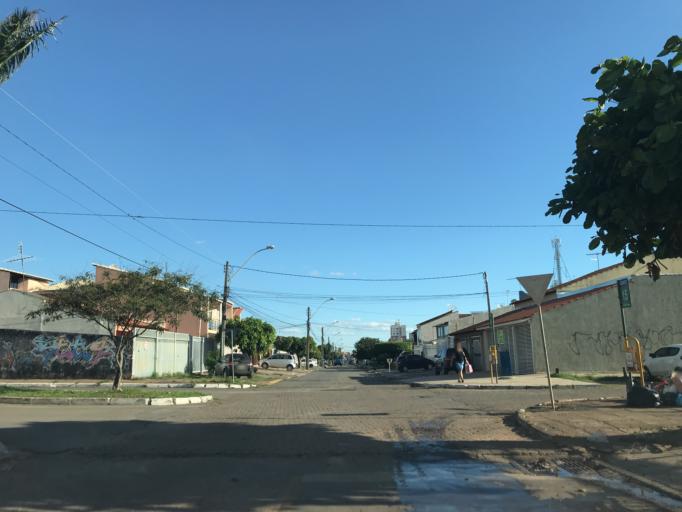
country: BR
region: Federal District
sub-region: Brasilia
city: Brasilia
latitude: -15.8131
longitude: -48.0632
